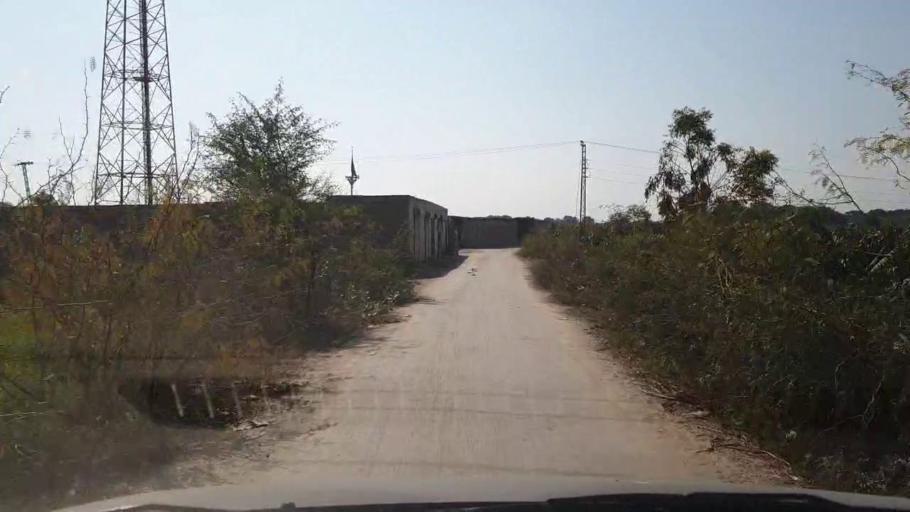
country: PK
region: Sindh
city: Tando Jam
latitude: 25.4496
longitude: 68.6249
